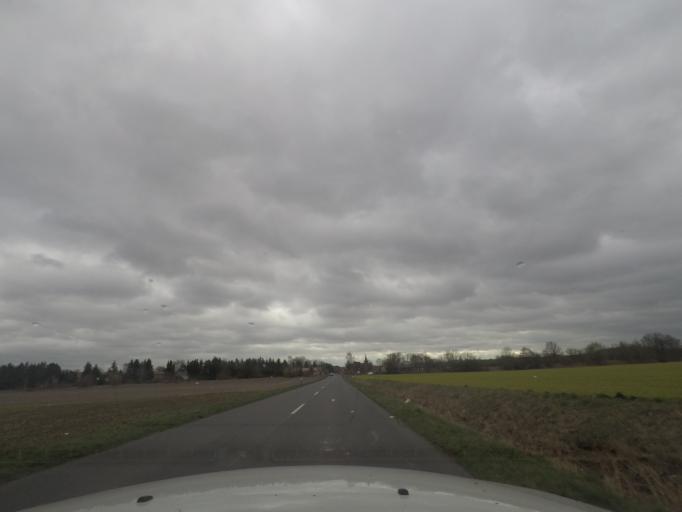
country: DE
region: Lower Saxony
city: Emmendorf
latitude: 53.0092
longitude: 10.6023
